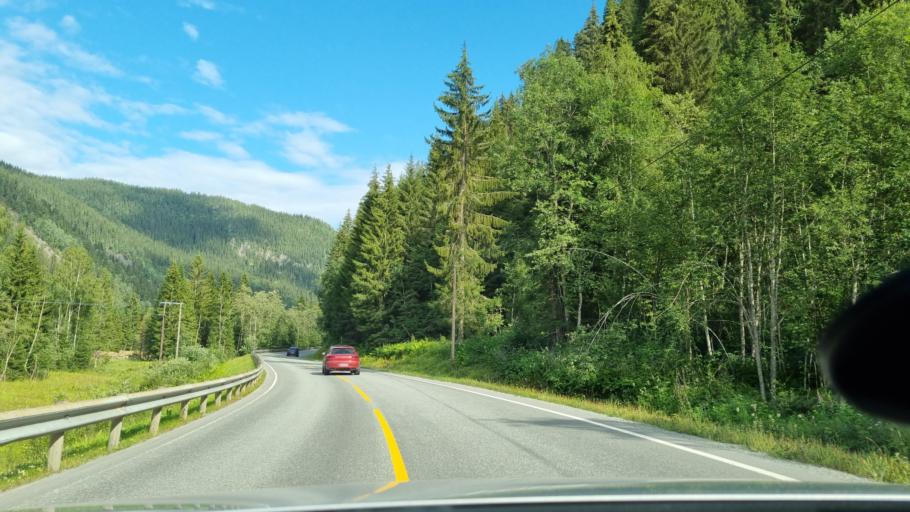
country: NO
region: Sor-Trondelag
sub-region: Midtre Gauldal
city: Storen
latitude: 62.9913
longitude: 10.5129
